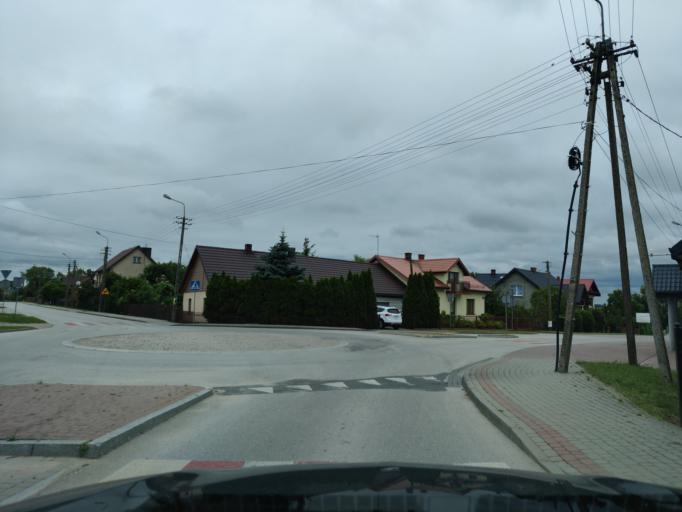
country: PL
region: Masovian Voivodeship
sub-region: Powiat makowski
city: Karniewo
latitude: 52.8353
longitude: 20.9894
